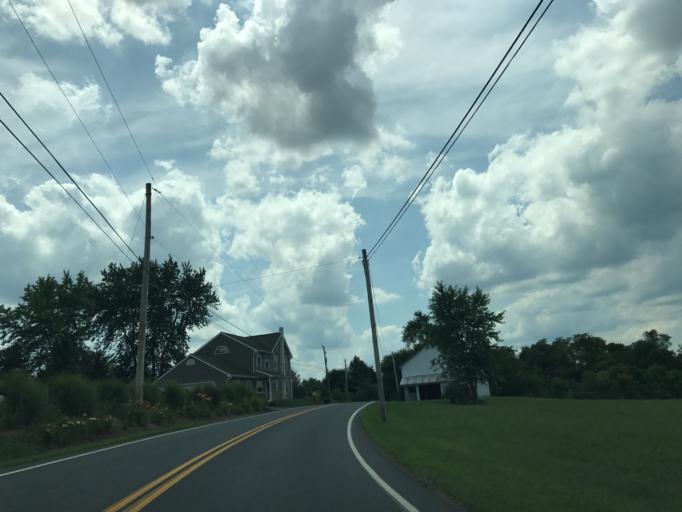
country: US
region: Pennsylvania
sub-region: Lancaster County
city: Manheim
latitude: 40.1838
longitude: -76.4611
